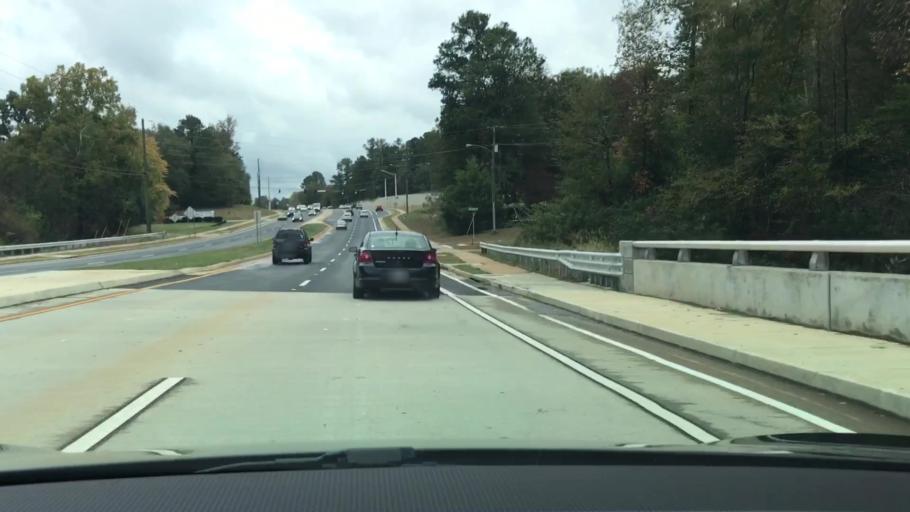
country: US
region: Georgia
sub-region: Oconee County
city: Watkinsville
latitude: 33.9021
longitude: -83.4634
